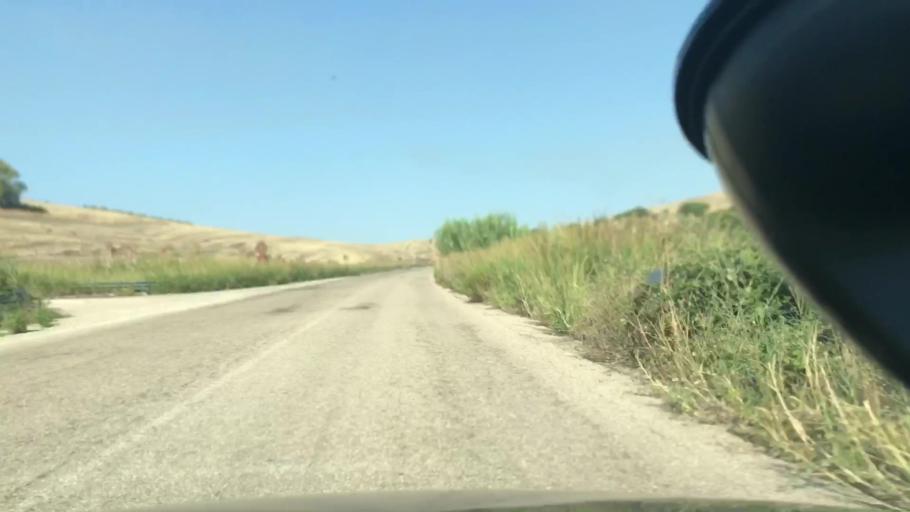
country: IT
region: Basilicate
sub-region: Provincia di Matera
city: Grottole
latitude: 40.6941
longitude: 16.4290
